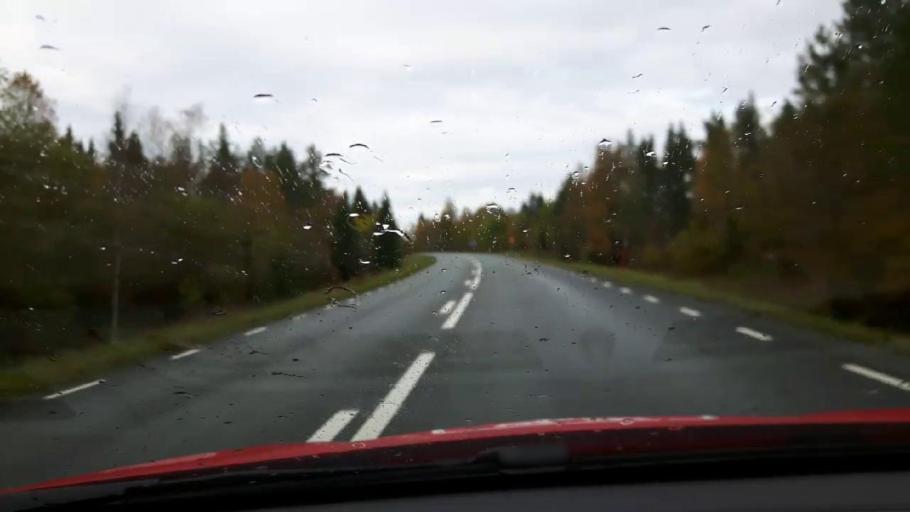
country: SE
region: Jaemtland
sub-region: Krokoms Kommun
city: Krokom
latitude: 63.0958
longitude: 14.3030
